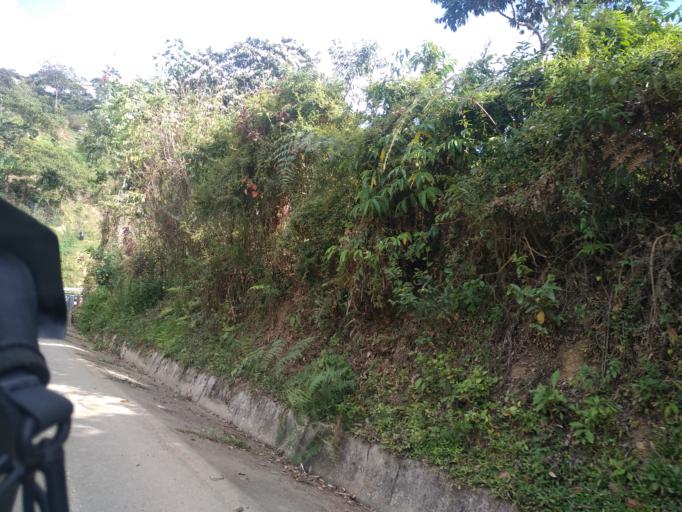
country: PE
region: Cajamarca
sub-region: Provincia de San Ignacio
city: San Ignacio
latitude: -5.1020
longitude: -79.0445
